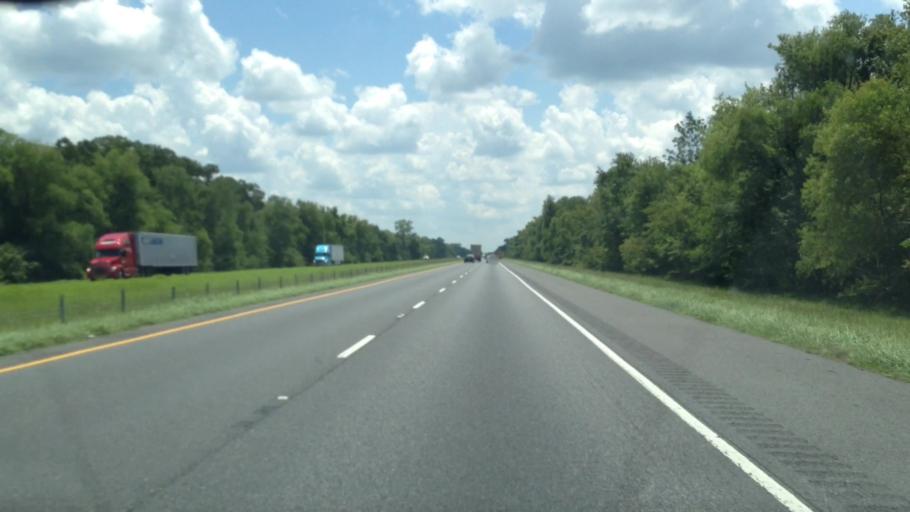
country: US
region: Louisiana
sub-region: Saint James Parish
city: Grand Point
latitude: 30.1416
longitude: -90.7529
